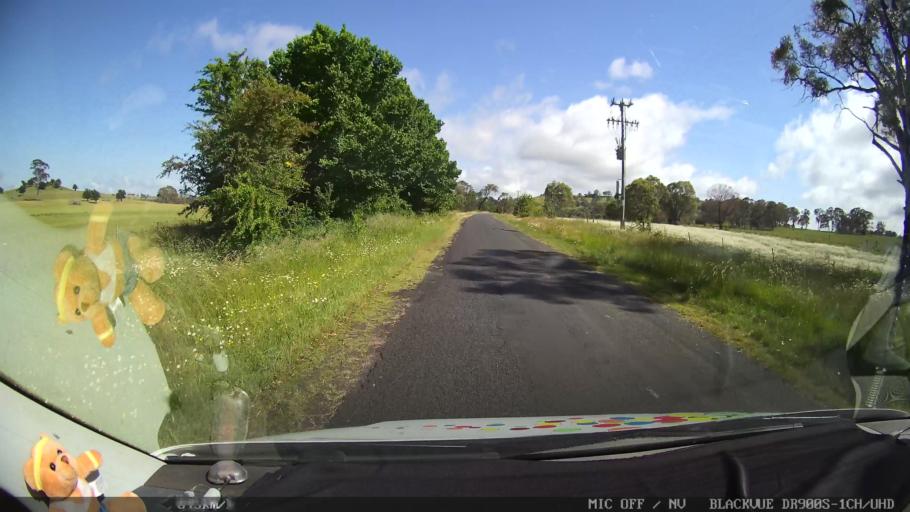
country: AU
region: New South Wales
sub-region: Guyra
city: Guyra
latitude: -30.0158
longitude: 151.6576
